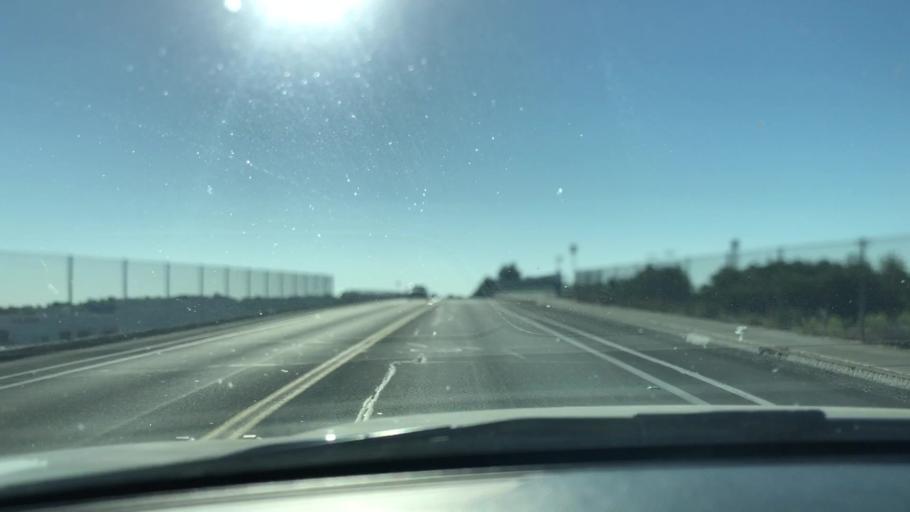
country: US
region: California
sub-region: Los Angeles County
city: Lancaster
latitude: 34.6677
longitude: -118.1544
